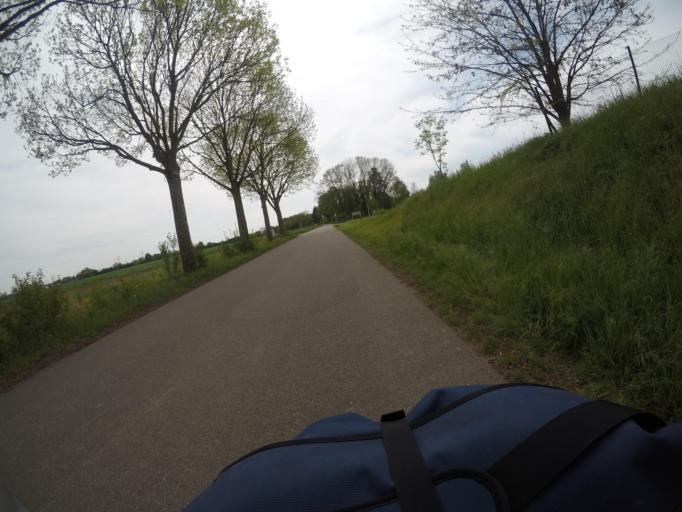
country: DE
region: Baden-Wuerttemberg
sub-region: Freiburg Region
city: Kehl
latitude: 48.5837
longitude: 7.8388
